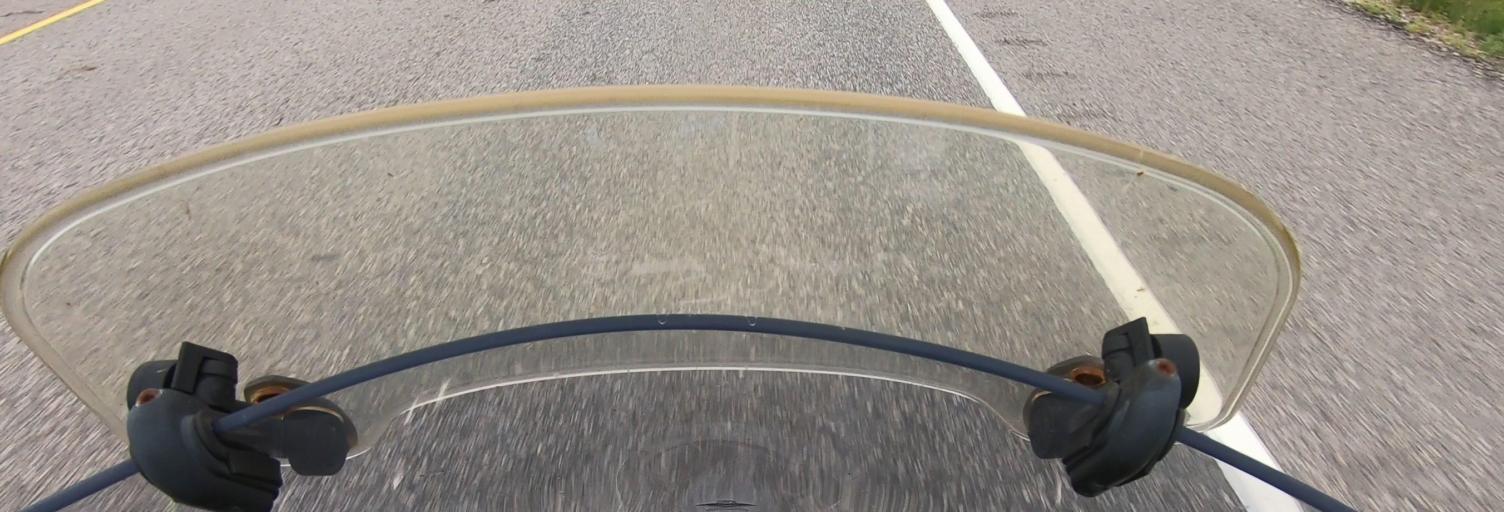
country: CA
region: Manitoba
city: Portage la Prairie
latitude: 49.9755
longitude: -98.6931
